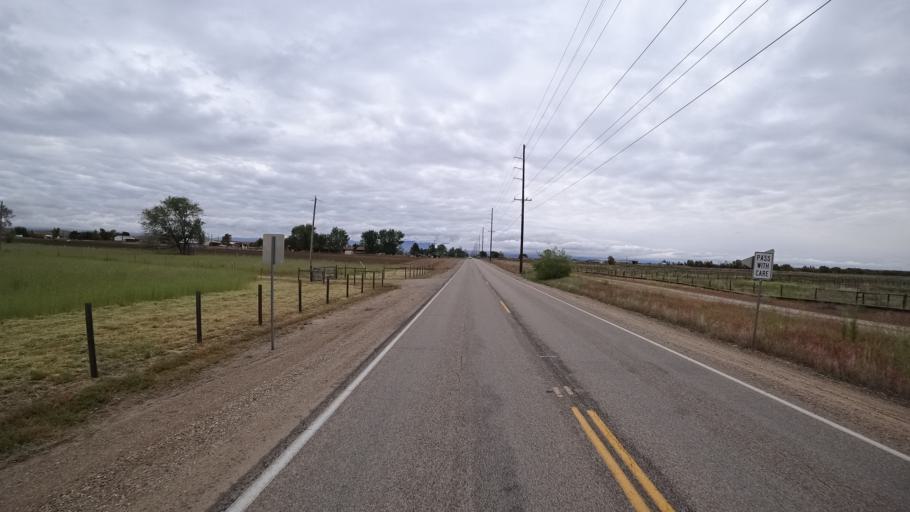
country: US
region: Idaho
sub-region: Ada County
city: Star
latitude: 43.7211
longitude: -116.4412
